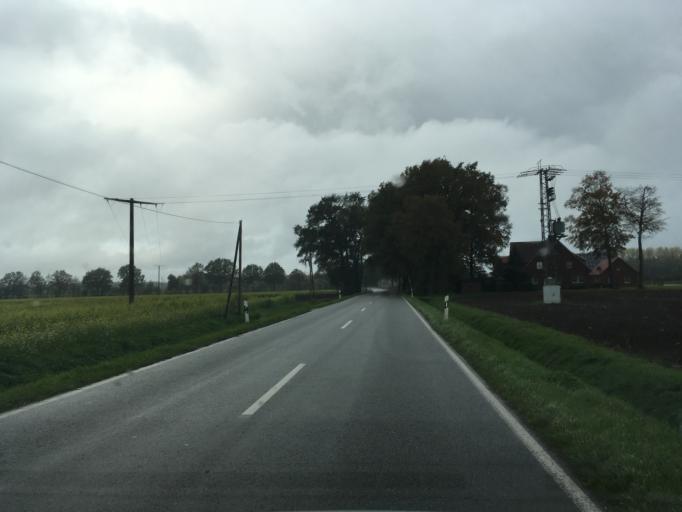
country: DE
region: North Rhine-Westphalia
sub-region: Regierungsbezirk Munster
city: Velen
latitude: 51.8658
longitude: 7.0322
